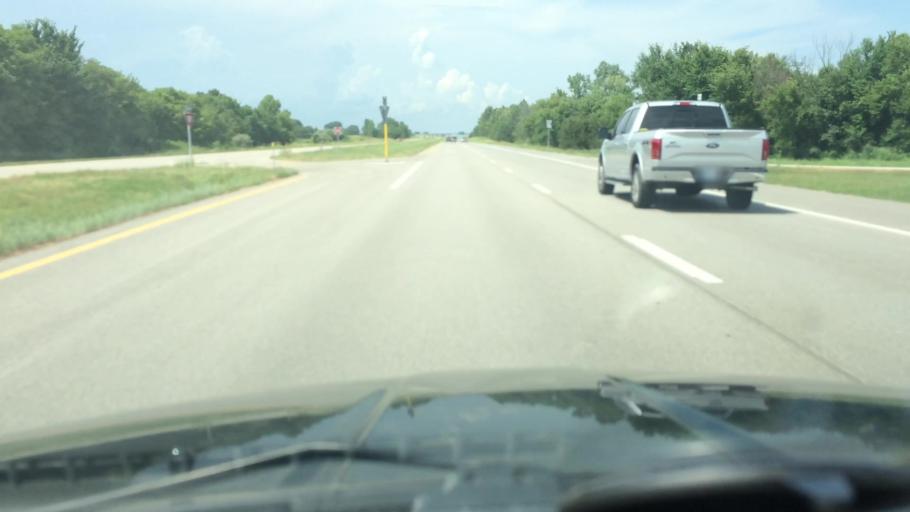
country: US
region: Missouri
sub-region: Henry County
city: Clinton
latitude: 38.2348
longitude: -93.7626
